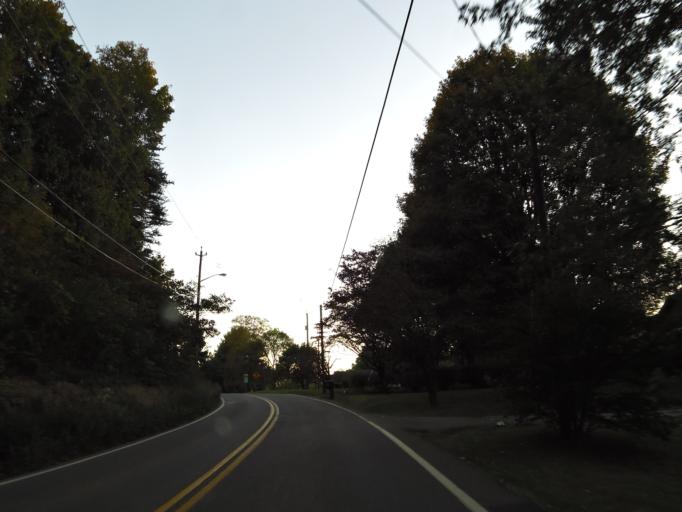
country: US
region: Tennessee
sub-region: Knox County
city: Knoxville
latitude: 36.0231
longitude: -83.9756
